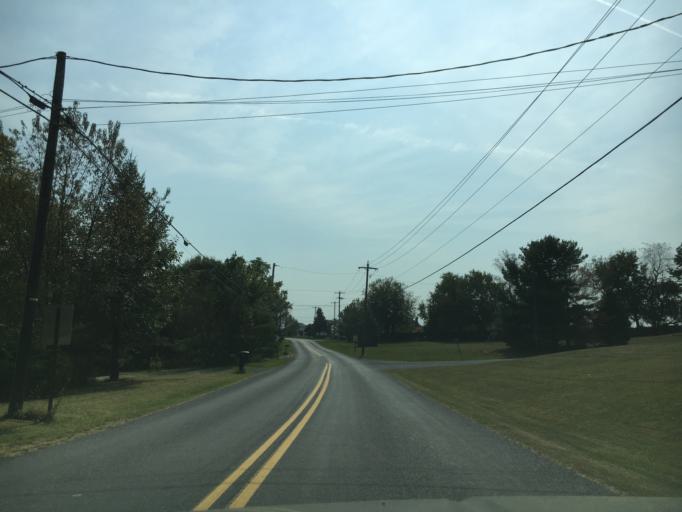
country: US
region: Pennsylvania
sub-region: Berks County
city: Topton
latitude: 40.5718
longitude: -75.7076
